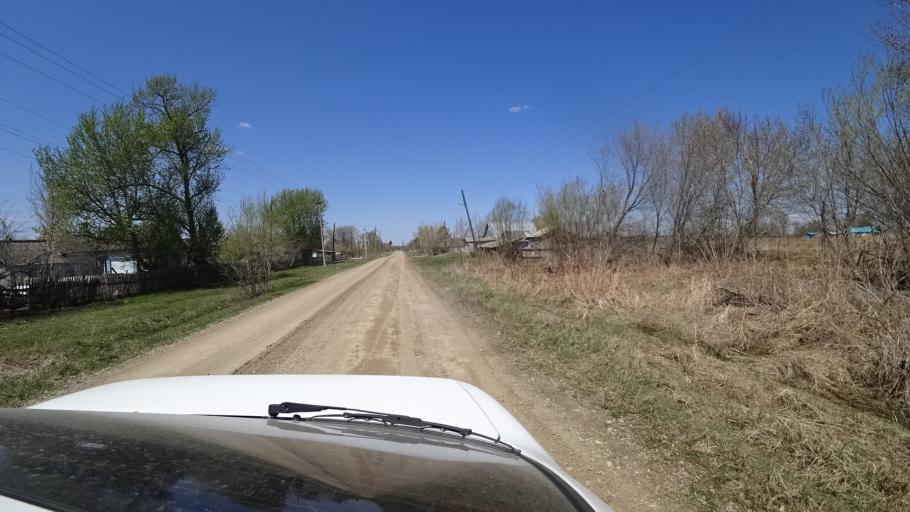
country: RU
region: Primorskiy
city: Lazo
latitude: 45.7974
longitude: 133.7646
